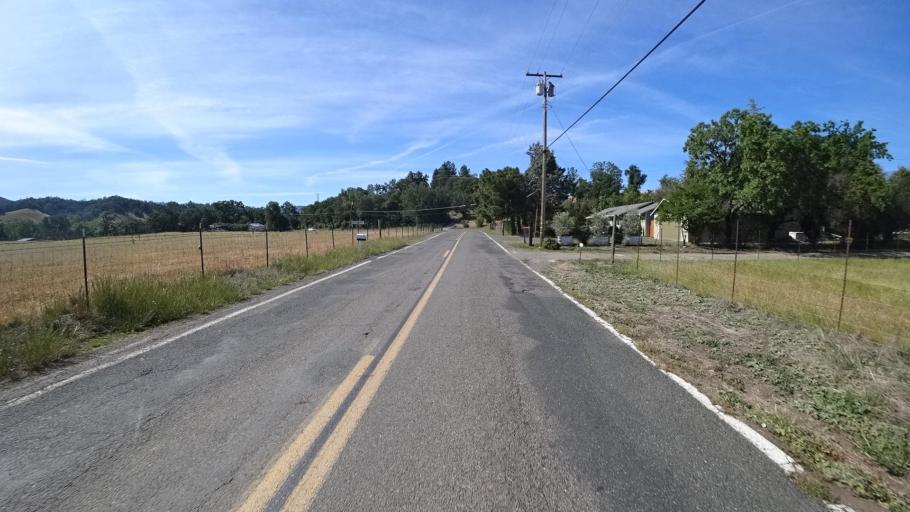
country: US
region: California
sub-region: Lake County
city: Kelseyville
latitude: 38.9647
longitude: -122.8386
